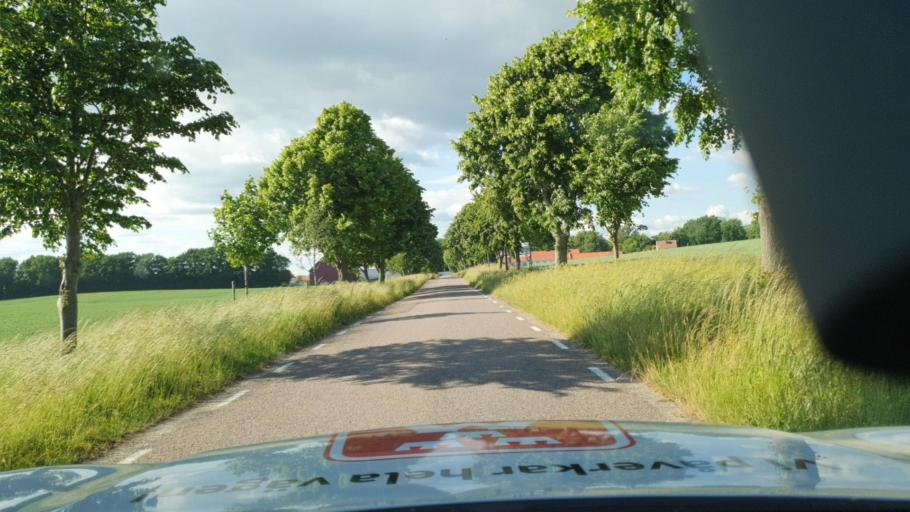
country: SE
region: Skane
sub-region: Ystads Kommun
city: Ystad
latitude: 55.4414
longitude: 13.7353
